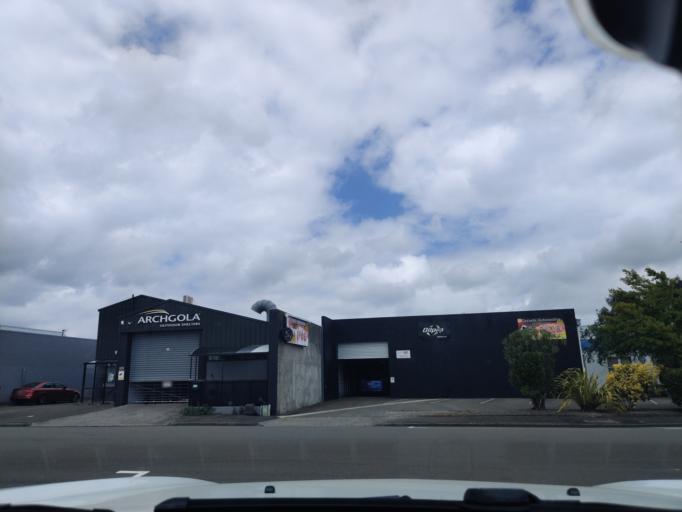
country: NZ
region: Manawatu-Wanganui
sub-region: Palmerston North City
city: Palmerston North
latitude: -40.3481
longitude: 175.5880
